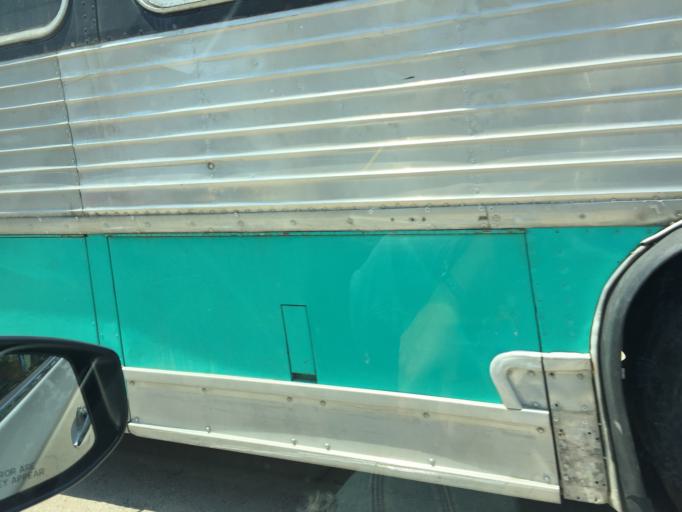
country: MX
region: Oaxaca
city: Asuncion Ixtaltepec
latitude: 16.5044
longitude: -95.0617
